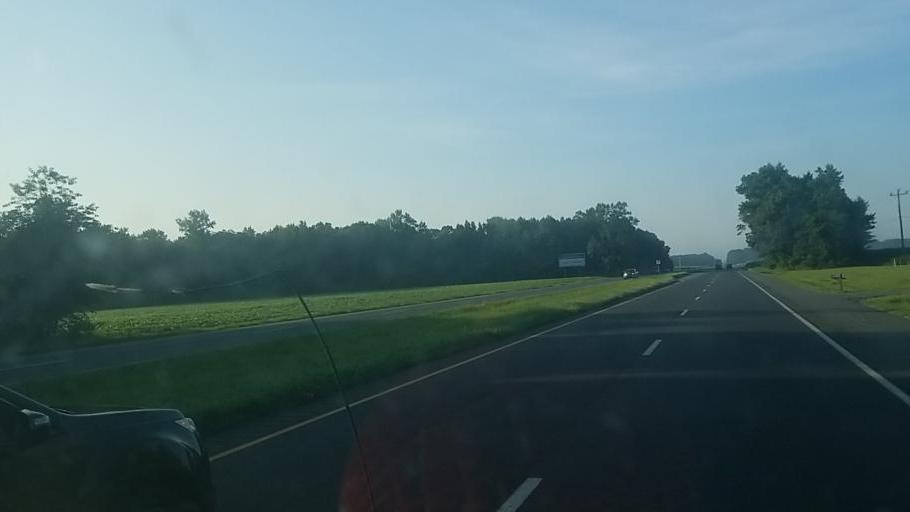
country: US
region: Delaware
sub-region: Sussex County
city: Selbyville
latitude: 38.4992
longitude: -75.2372
